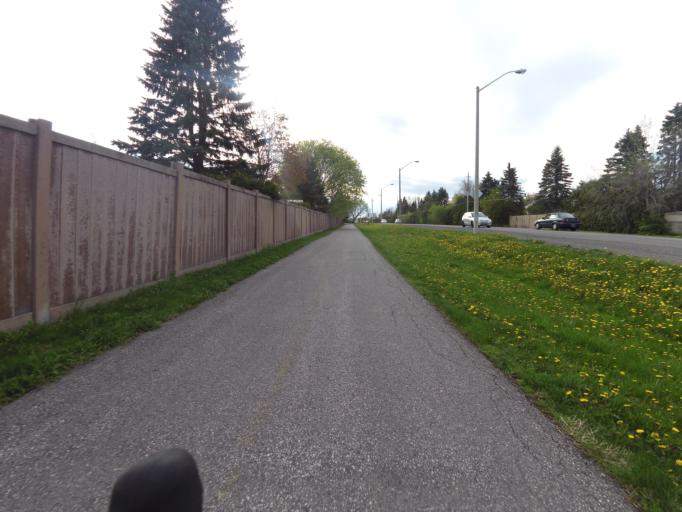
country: CA
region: Ontario
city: Bells Corners
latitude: 45.2741
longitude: -75.7655
